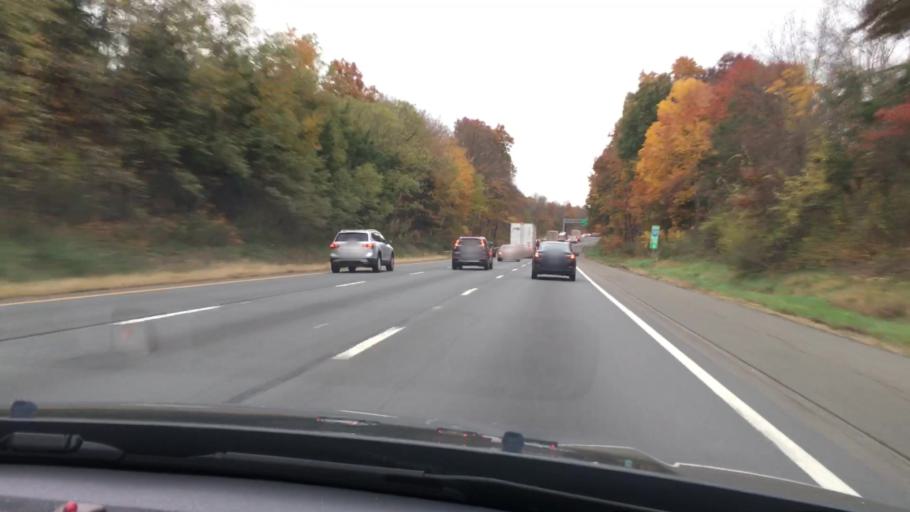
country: US
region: New Jersey
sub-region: Somerset County
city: Bernardsville
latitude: 40.7358
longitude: -74.5367
